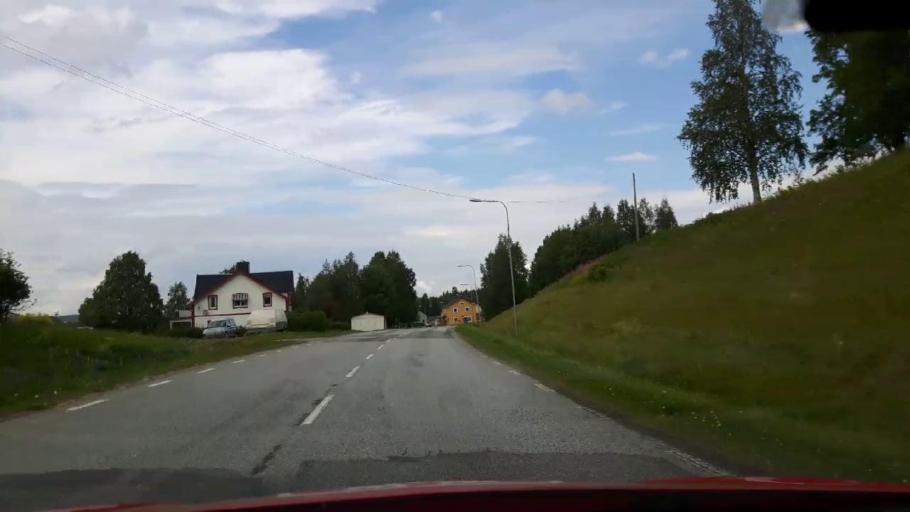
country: SE
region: Jaemtland
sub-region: Stroemsunds Kommun
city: Stroemsund
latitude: 64.4321
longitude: 15.5957
